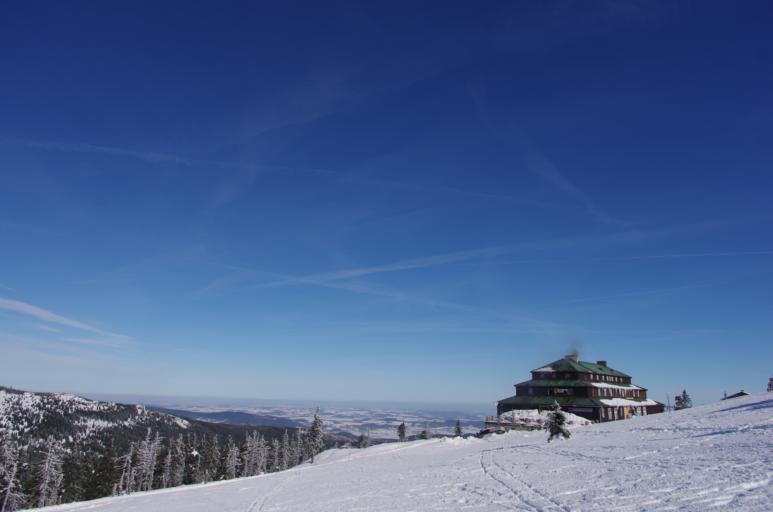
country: CZ
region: Kralovehradecky
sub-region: Okres Trutnov
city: Spindleruv Mlyn
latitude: 50.7631
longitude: 15.6391
